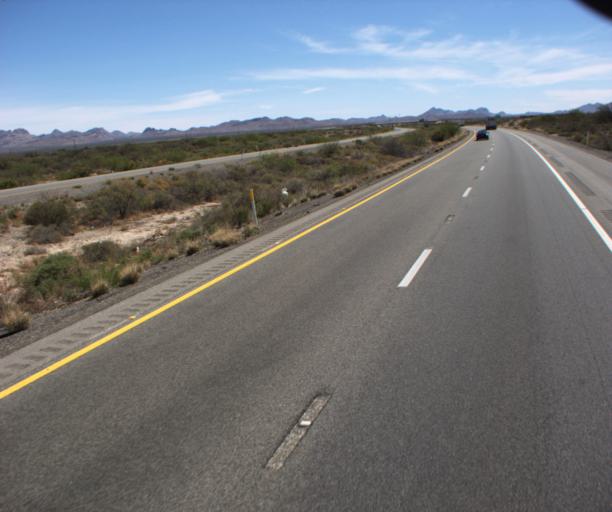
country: US
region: New Mexico
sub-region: Hidalgo County
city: Lordsburg
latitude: 32.2576
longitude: -109.2038
